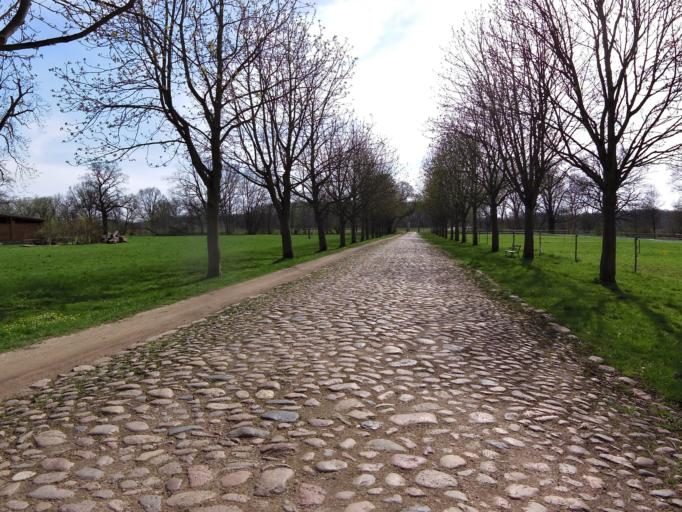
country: DE
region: Saxony
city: Schkeuditz
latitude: 51.3779
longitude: 12.2799
